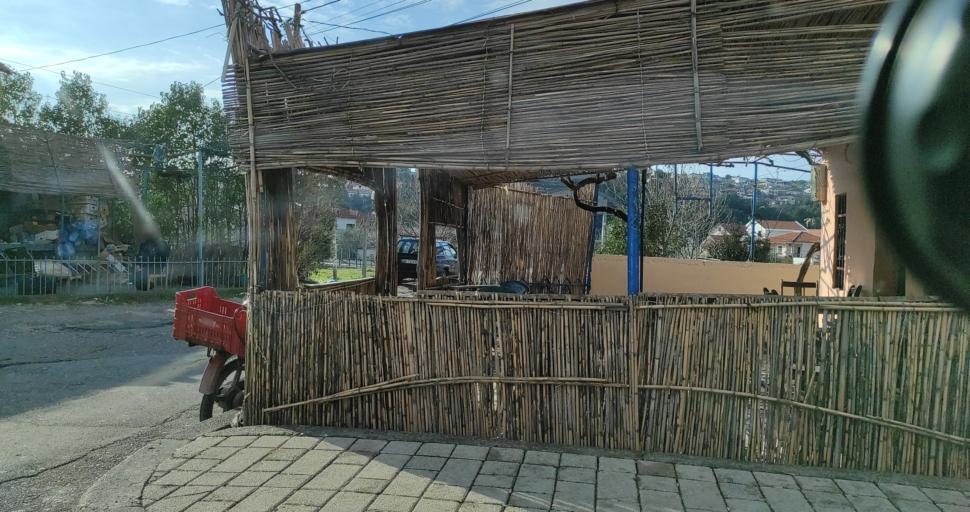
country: AL
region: Lezhe
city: Lezhe
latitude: 41.7854
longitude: 19.6437
